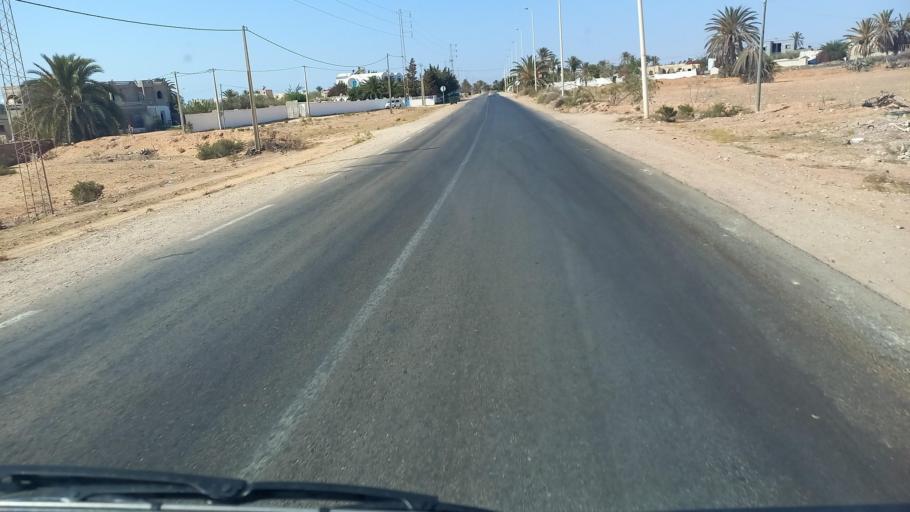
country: TN
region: Madanin
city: Midoun
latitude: 33.7750
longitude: 11.0292
